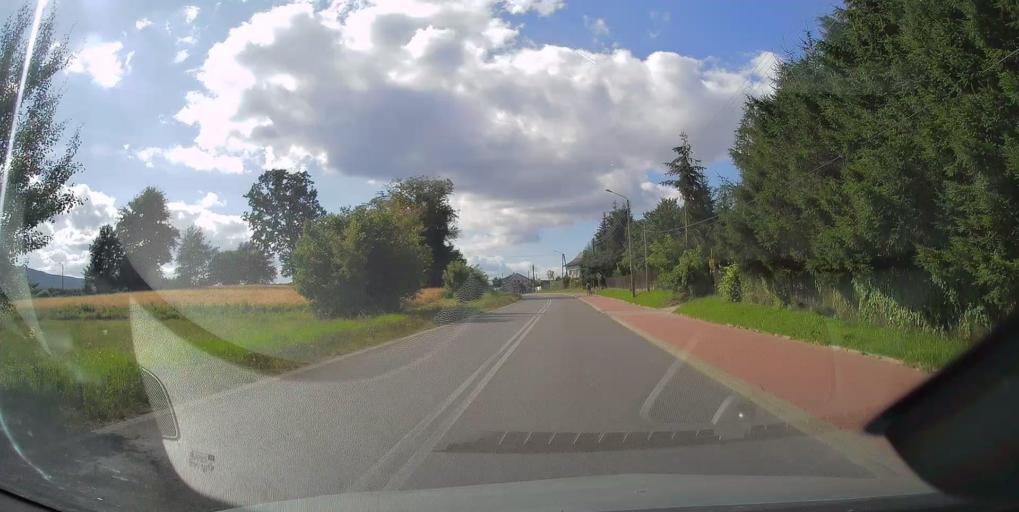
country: PL
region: Swietokrzyskie
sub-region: Powiat kielecki
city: Nowa Slupia
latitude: 50.8804
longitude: 21.0613
